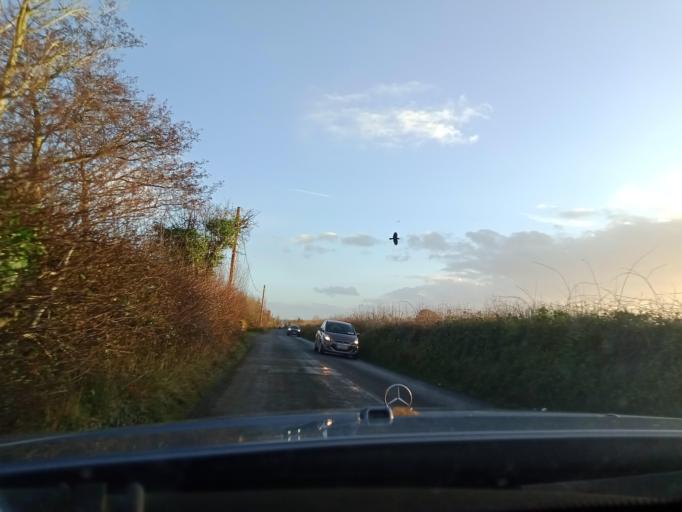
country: IE
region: Leinster
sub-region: Kilkenny
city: Callan
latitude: 52.5030
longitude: -7.3438
